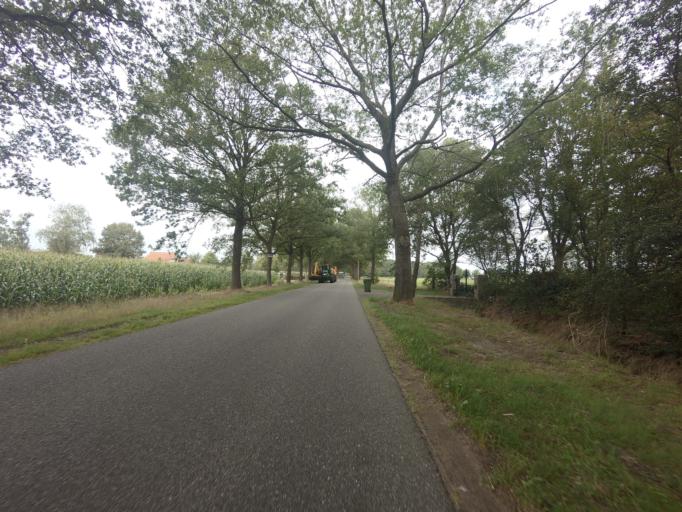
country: NL
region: Friesland
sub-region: Gemeente Heerenveen
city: Jubbega
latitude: 52.9664
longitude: 6.1967
